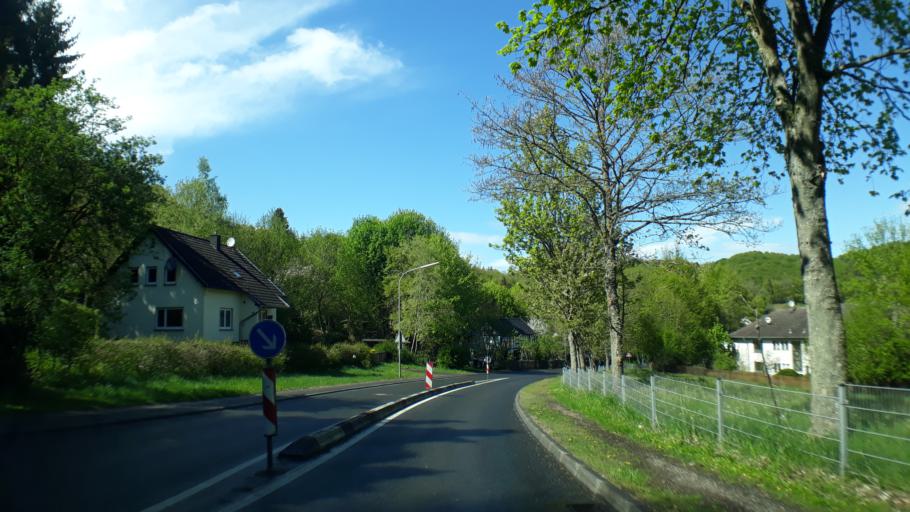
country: DE
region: North Rhine-Westphalia
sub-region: Regierungsbezirk Koln
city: Kall
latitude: 50.5085
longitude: 6.5741
